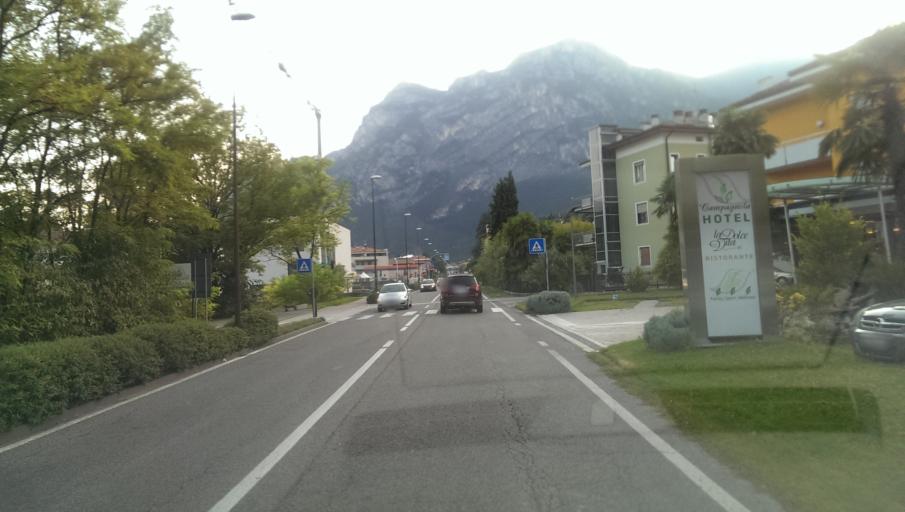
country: IT
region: Trentino-Alto Adige
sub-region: Provincia di Trento
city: Riva del Garda
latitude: 45.9021
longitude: 10.8596
